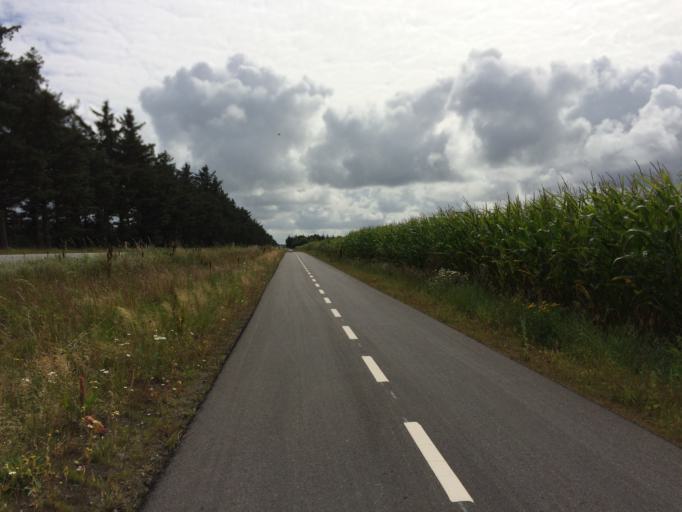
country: DK
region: Central Jutland
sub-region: Holstebro Kommune
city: Ulfborg
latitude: 56.3064
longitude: 8.3385
